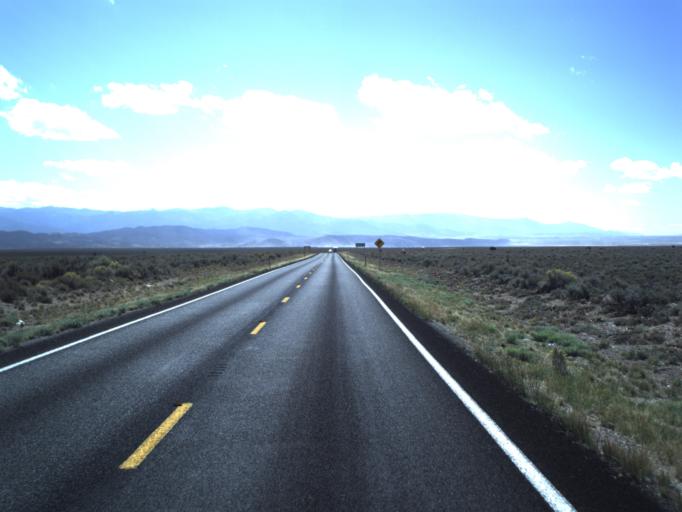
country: US
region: Utah
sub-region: Iron County
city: Enoch
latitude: 38.0087
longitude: -112.9979
